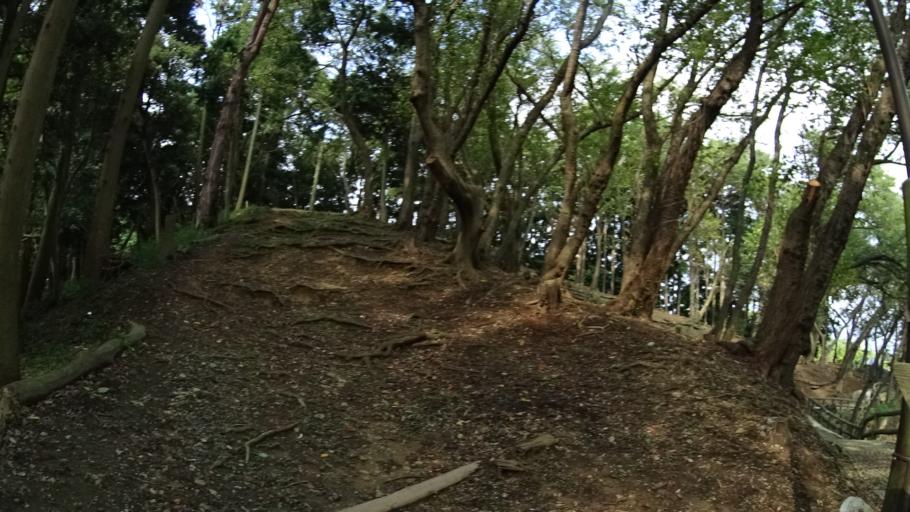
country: JP
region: Kanagawa
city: Yokosuka
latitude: 35.2839
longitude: 139.6289
